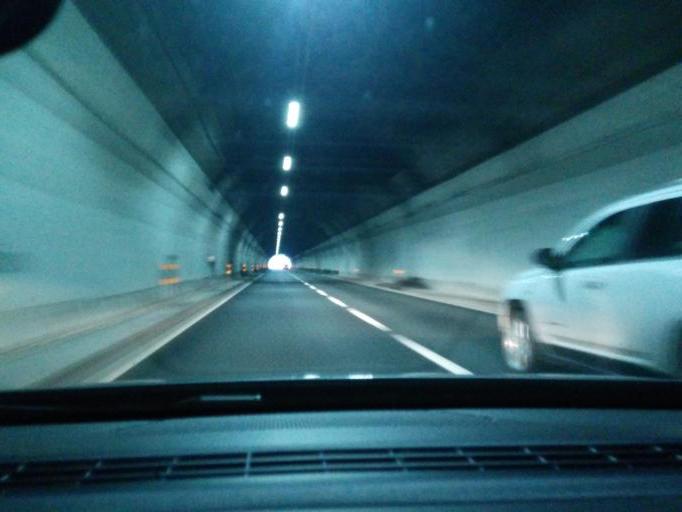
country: IT
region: Liguria
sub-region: Provincia di Savona
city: Varazze
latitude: 44.3662
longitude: 8.5696
